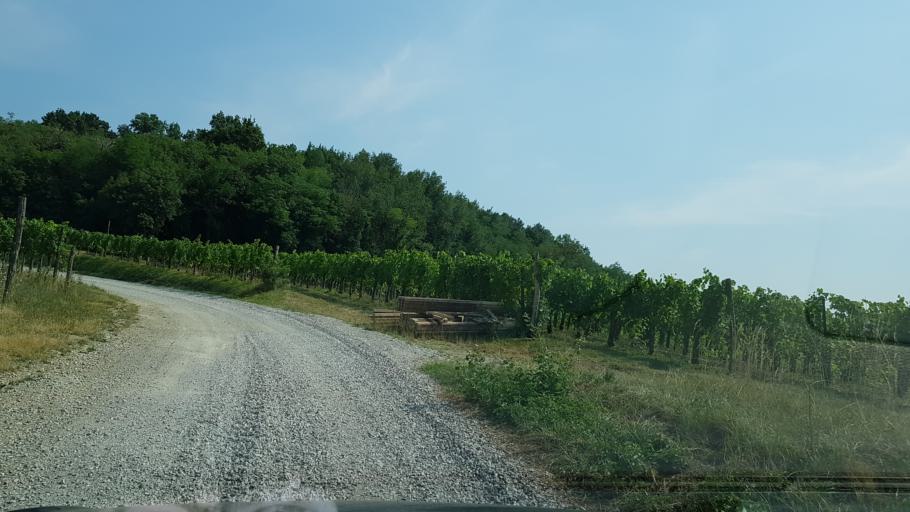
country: SI
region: Brda
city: Dobrovo
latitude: 45.9939
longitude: 13.5164
